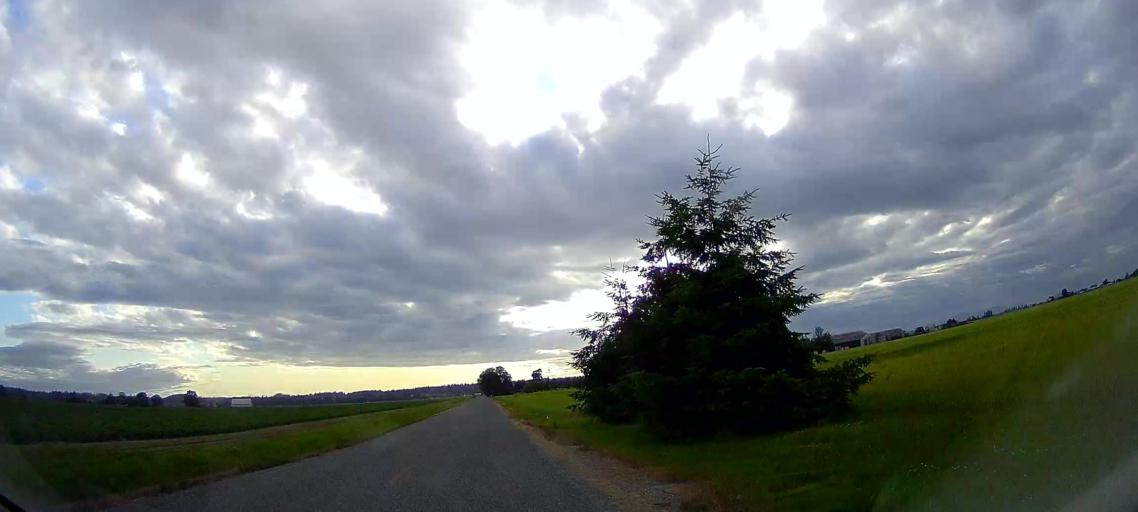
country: US
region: Washington
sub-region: Skagit County
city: Mount Vernon
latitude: 48.3848
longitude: -122.3893
